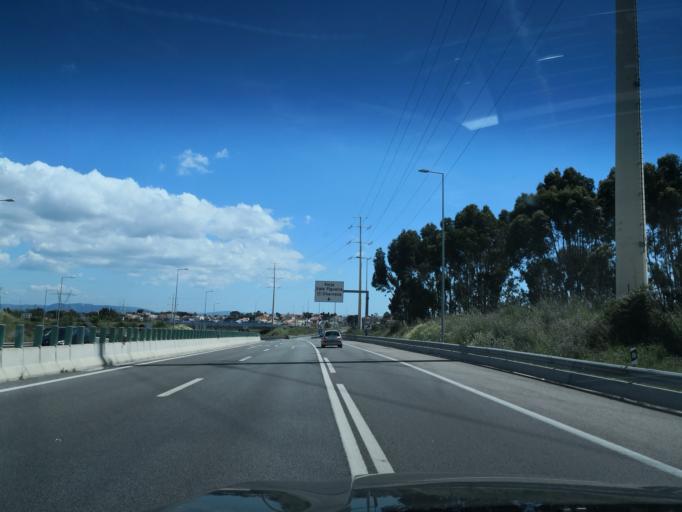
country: PT
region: Setubal
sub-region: Almada
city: Charneca
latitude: 38.6262
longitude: -9.1925
